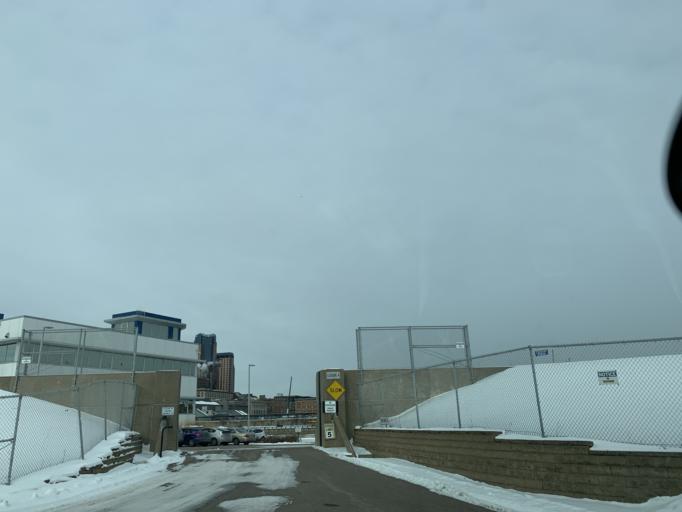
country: US
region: Minnesota
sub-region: Ramsey County
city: Saint Paul
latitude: 44.9448
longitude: -93.0795
